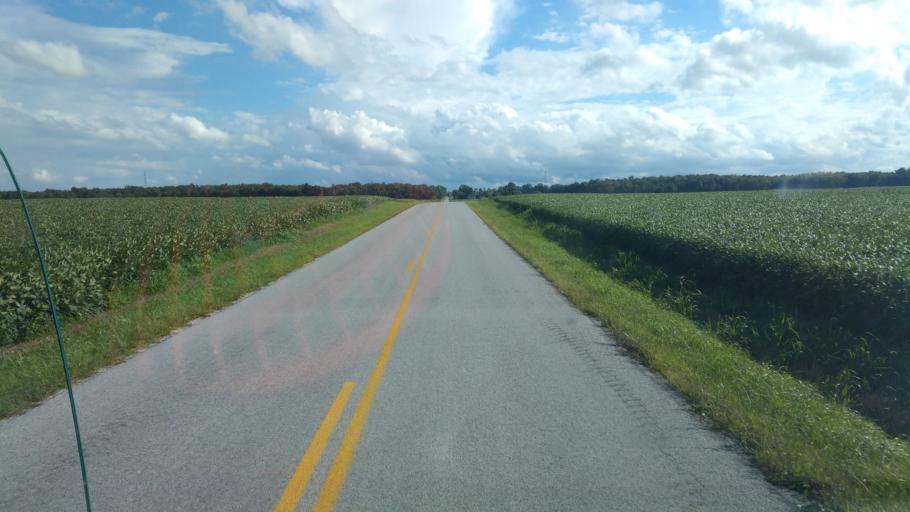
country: US
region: Ohio
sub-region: Hardin County
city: Kenton
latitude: 40.6779
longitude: -83.6337
